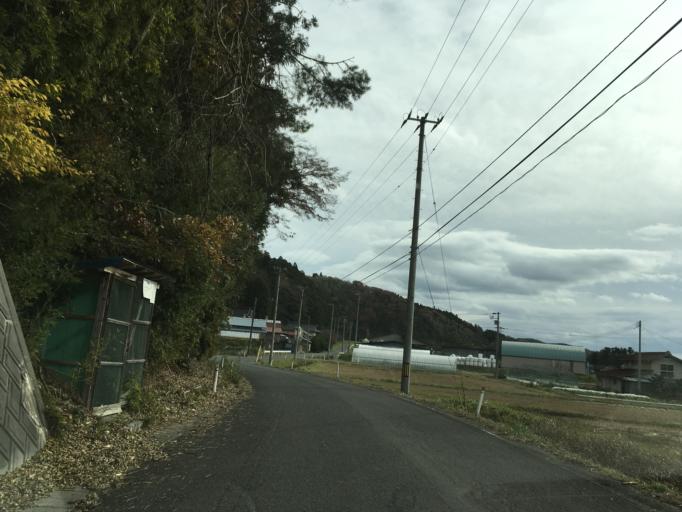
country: JP
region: Iwate
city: Ichinoseki
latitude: 38.7694
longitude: 141.2709
